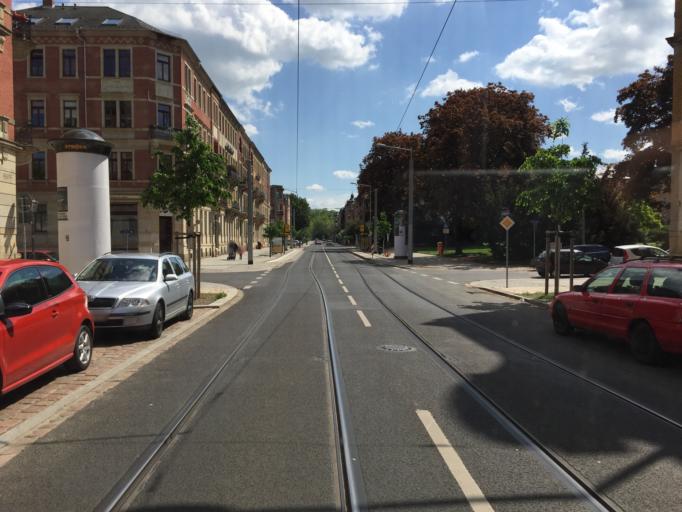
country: DE
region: Saxony
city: Dresden
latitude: 51.0467
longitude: 13.6929
